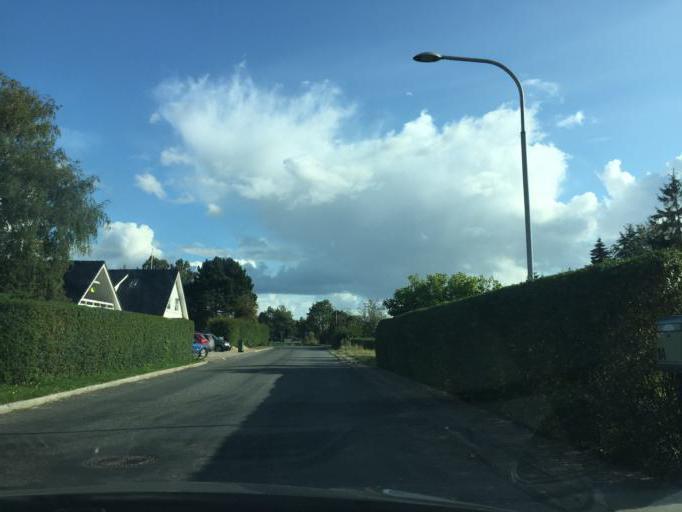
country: DK
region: South Denmark
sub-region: Kerteminde Kommune
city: Langeskov
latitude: 55.3152
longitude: 10.5317
